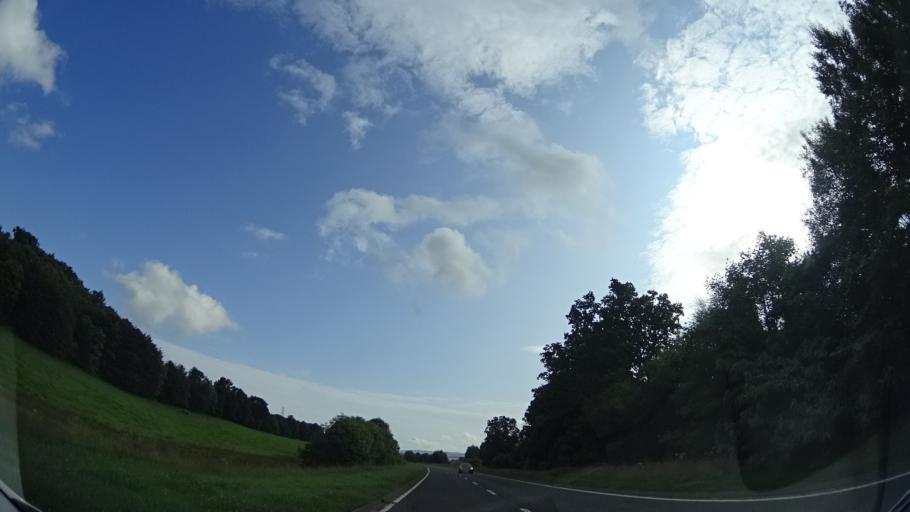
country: GB
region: Scotland
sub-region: Highland
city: Conon Bridge
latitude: 57.5719
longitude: -4.4570
